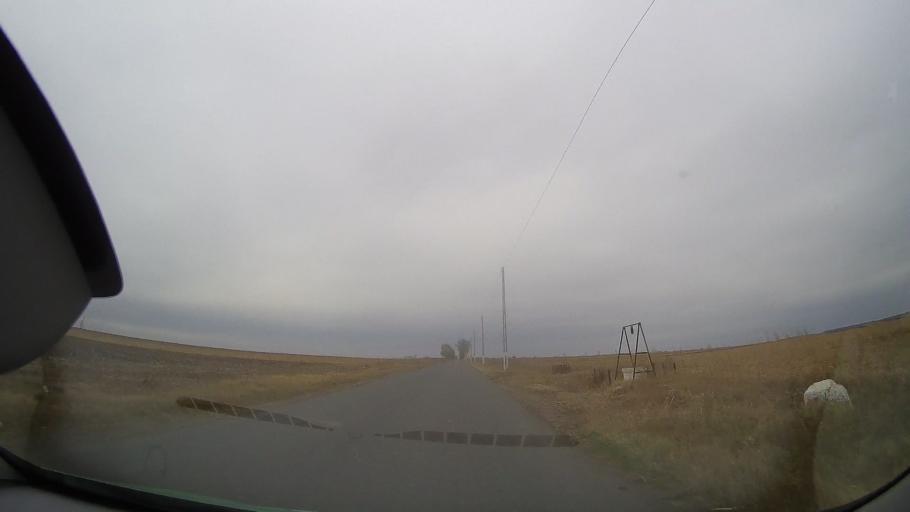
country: RO
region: Braila
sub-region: Comuna Budesti
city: Tataru
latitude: 44.8607
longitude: 27.4248
